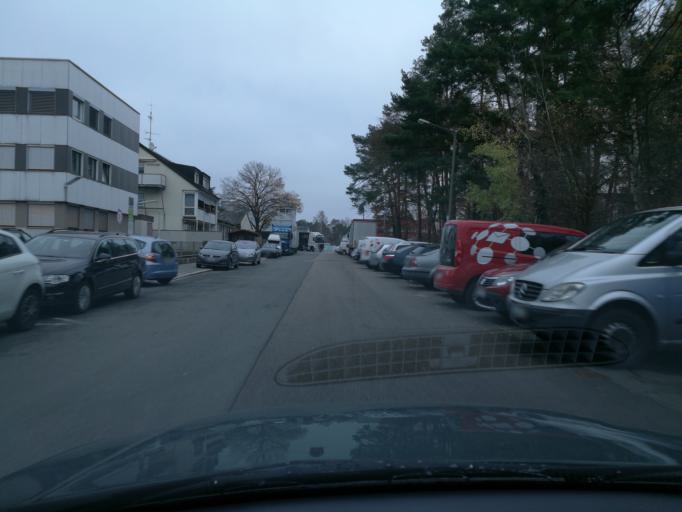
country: DE
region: Bavaria
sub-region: Regierungsbezirk Mittelfranken
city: Feucht
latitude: 49.4142
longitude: 11.1650
